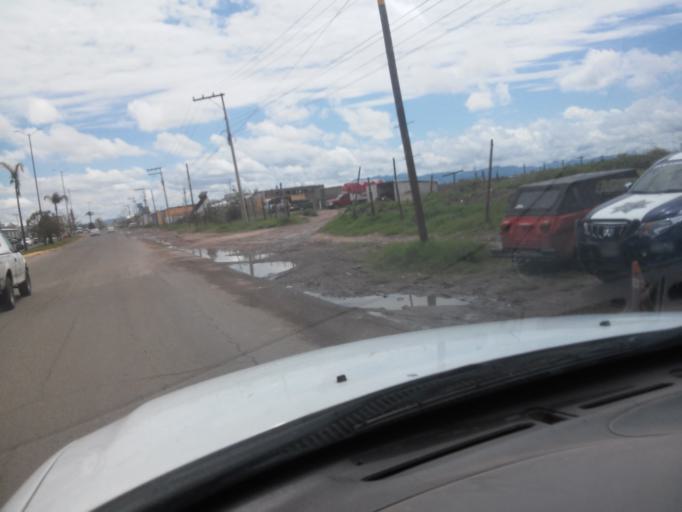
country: MX
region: Durango
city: Victoria de Durango
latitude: 24.0300
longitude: -104.6093
